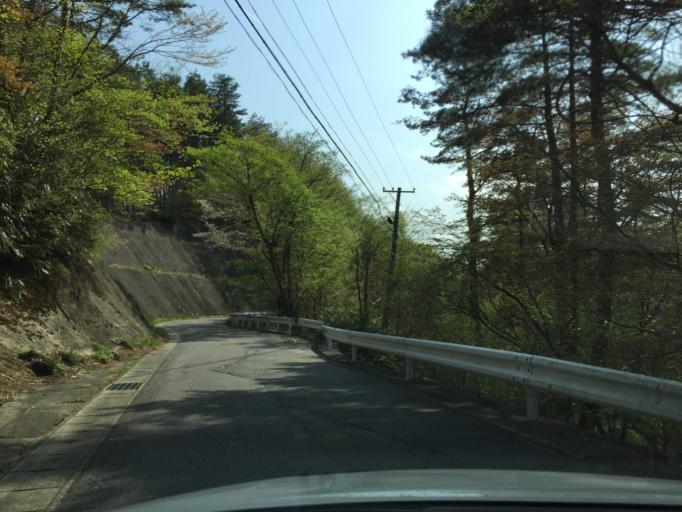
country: JP
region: Fukushima
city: Iwaki
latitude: 37.1902
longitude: 140.8507
